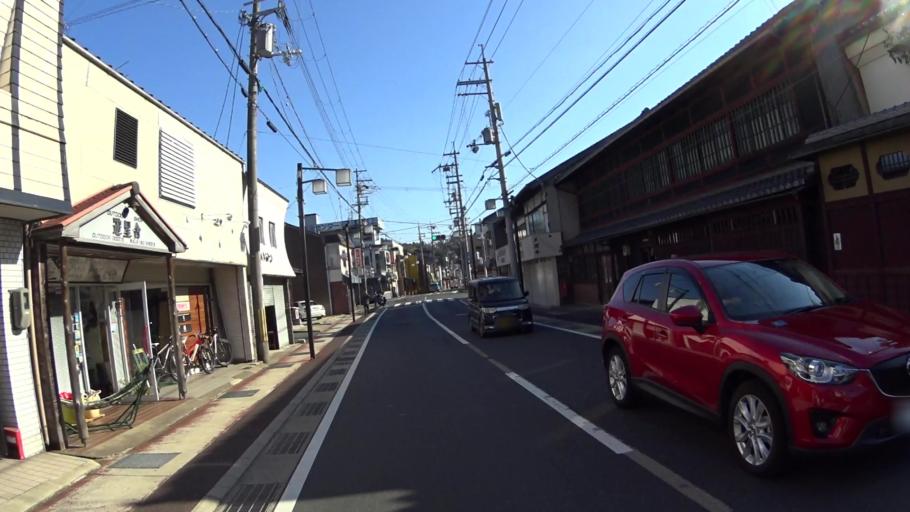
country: JP
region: Kyoto
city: Miyazu
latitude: 35.6245
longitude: 135.0584
